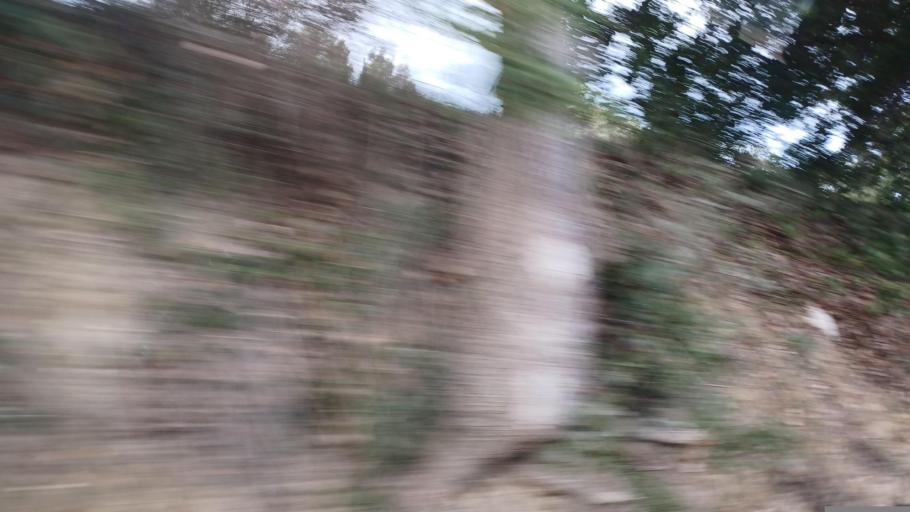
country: CY
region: Pafos
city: Tala
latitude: 34.8922
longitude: 32.4781
